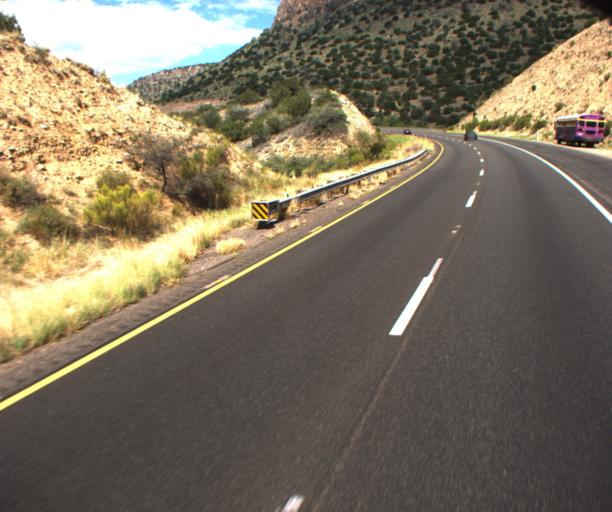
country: US
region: Arizona
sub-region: Yavapai County
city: Camp Verde
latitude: 34.5387
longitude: -111.9209
